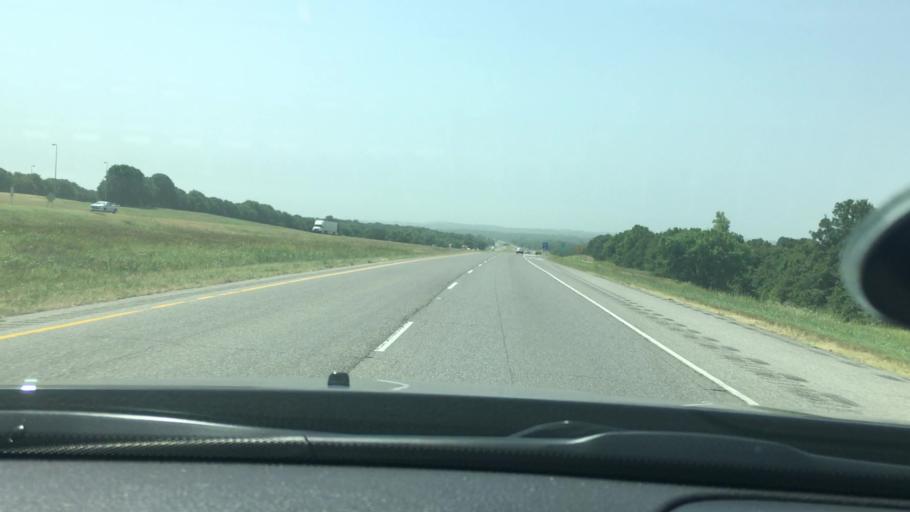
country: US
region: Oklahoma
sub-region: Murray County
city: Davis
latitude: 34.5538
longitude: -97.1919
